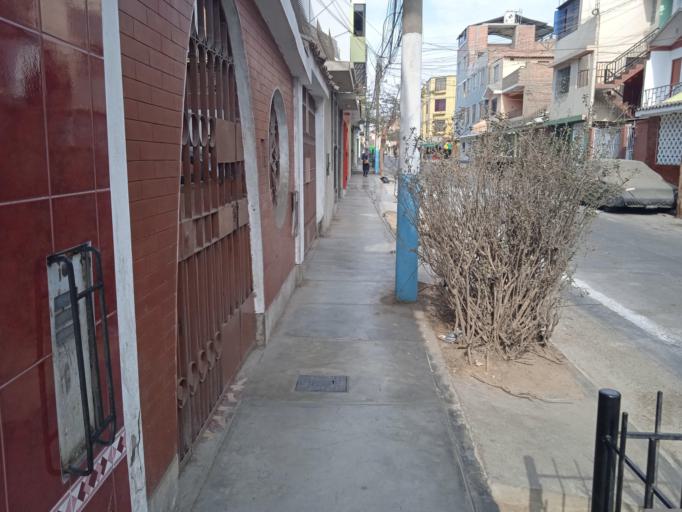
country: PE
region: Callao
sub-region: Callao
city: Callao
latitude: -12.0102
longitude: -77.0962
